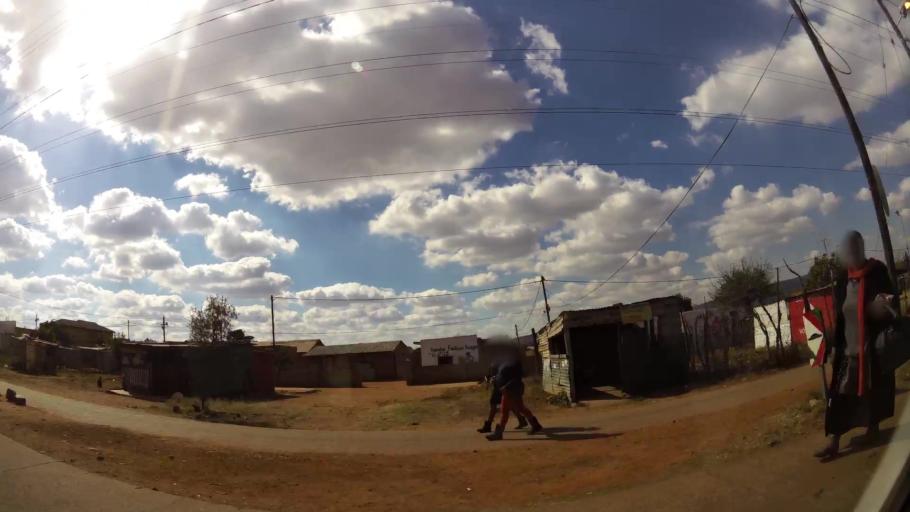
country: ZA
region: Gauteng
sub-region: City of Tshwane Metropolitan Municipality
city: Cullinan
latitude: -25.7054
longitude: 28.3948
